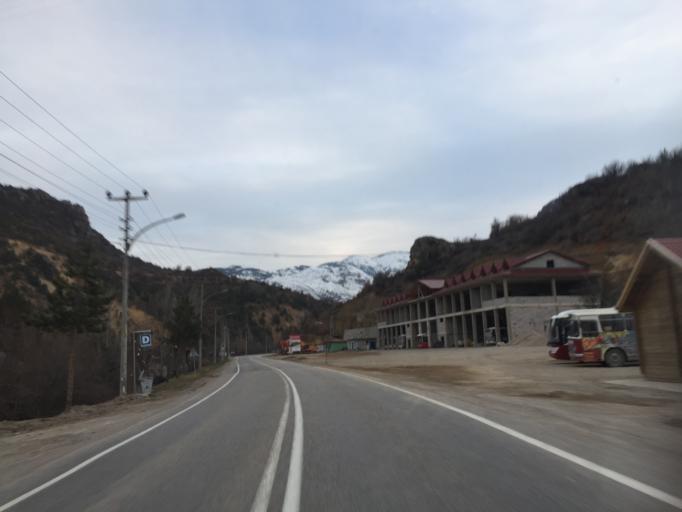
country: TR
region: Gumushane
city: Gumushkhane
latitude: 40.4830
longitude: 39.4622
